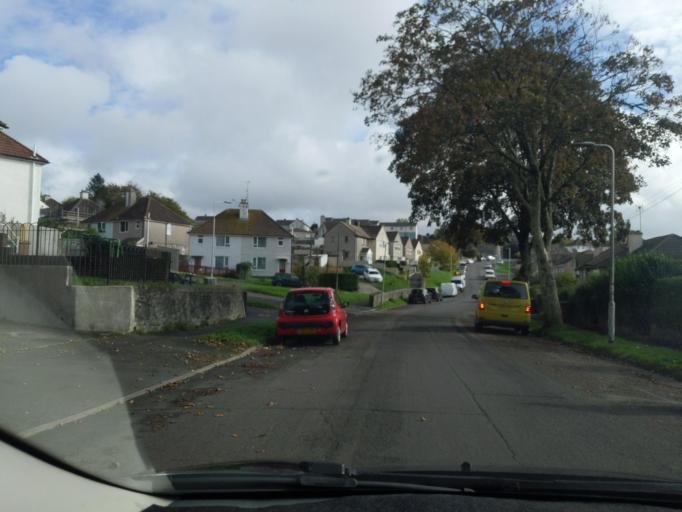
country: GB
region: England
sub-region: Cornwall
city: Torpoint
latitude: 50.4057
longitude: -4.1811
